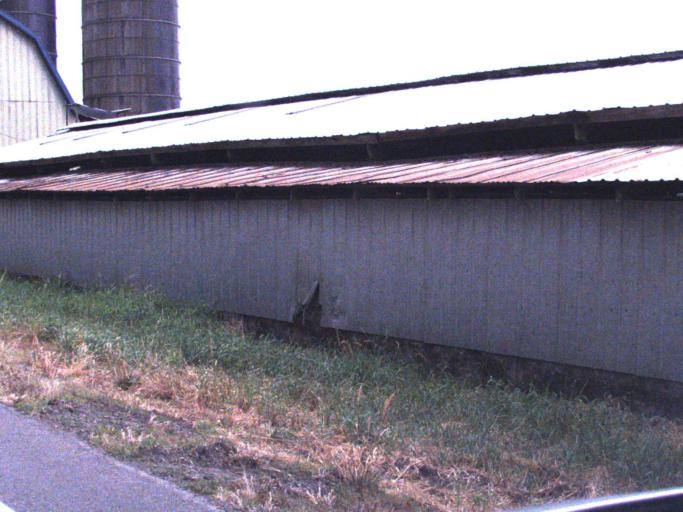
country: US
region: Washington
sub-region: King County
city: Duvall
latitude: 47.7748
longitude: -121.9588
